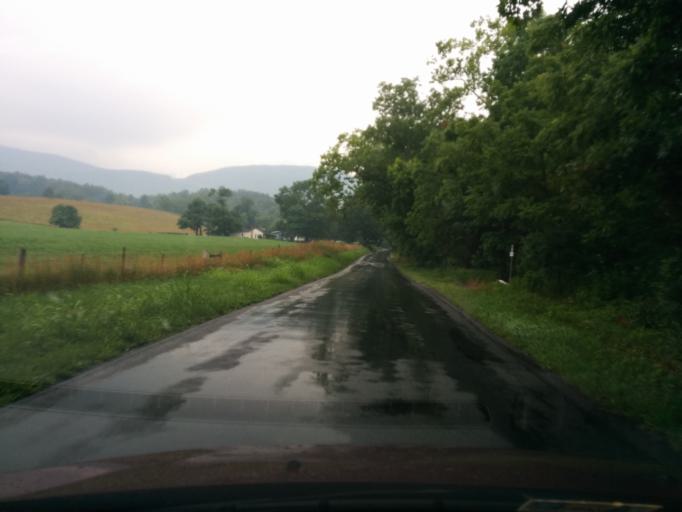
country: US
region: Virginia
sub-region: Rockbridge County
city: East Lexington
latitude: 37.9026
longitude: -79.4158
